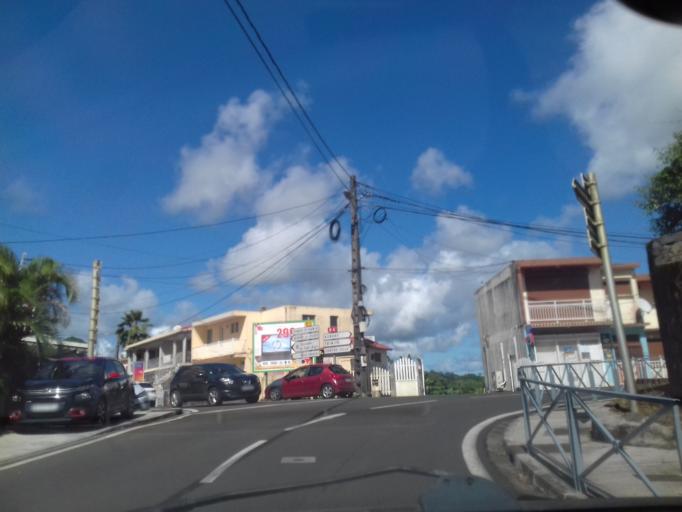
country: MQ
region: Martinique
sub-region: Martinique
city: Le Gros-Morne
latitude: 14.7132
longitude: -61.0120
